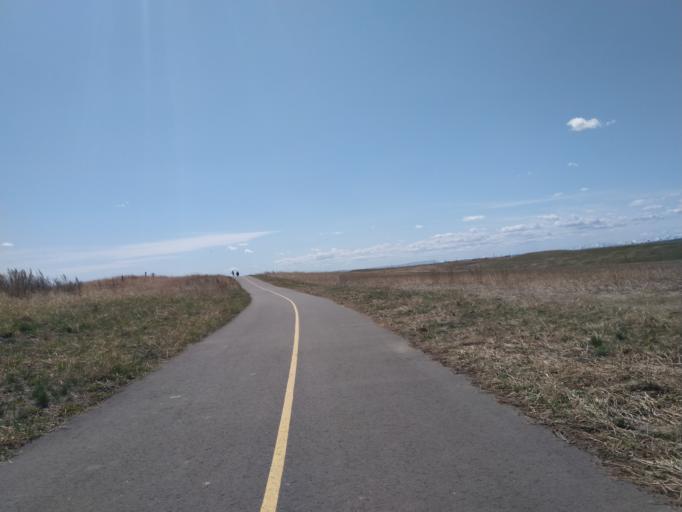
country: CA
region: Alberta
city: Chestermere
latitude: 51.0325
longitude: -113.9237
